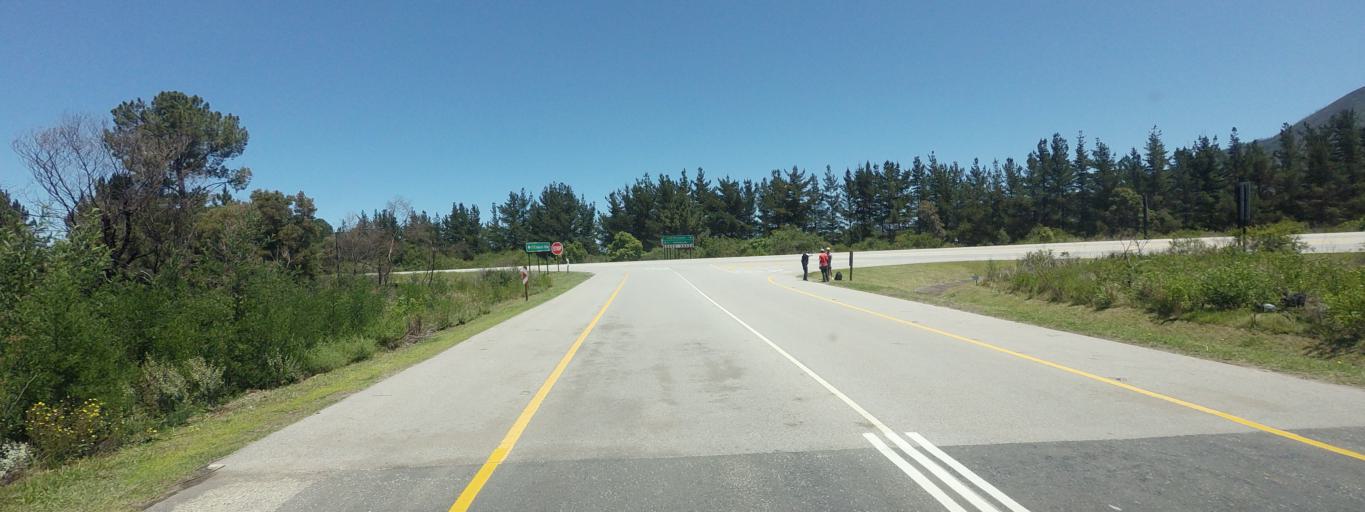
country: ZA
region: Western Cape
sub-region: Eden District Municipality
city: Plettenberg Bay
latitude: -33.9382
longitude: 23.4906
